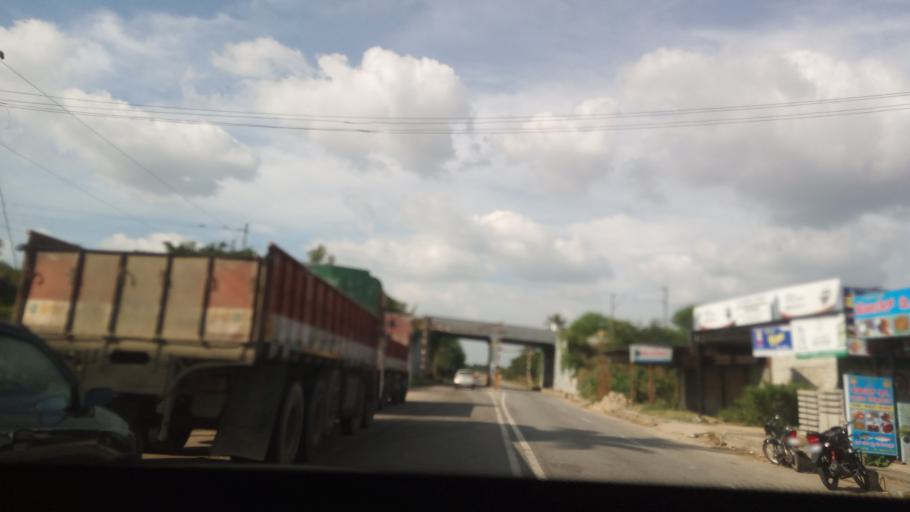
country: IN
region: Karnataka
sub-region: Mandya
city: Maddur
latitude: 12.6138
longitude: 77.0580
